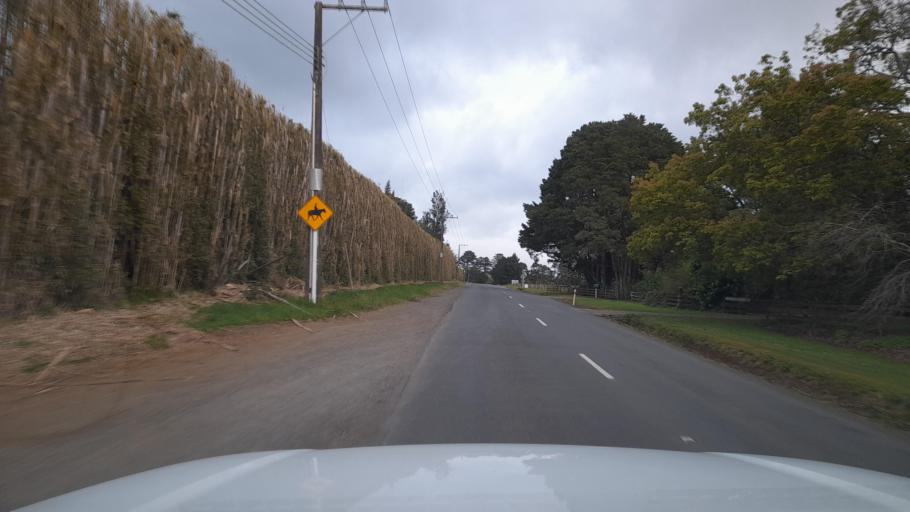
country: NZ
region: Northland
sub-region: Whangarei
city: Maungatapere
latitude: -35.7475
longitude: 174.2118
